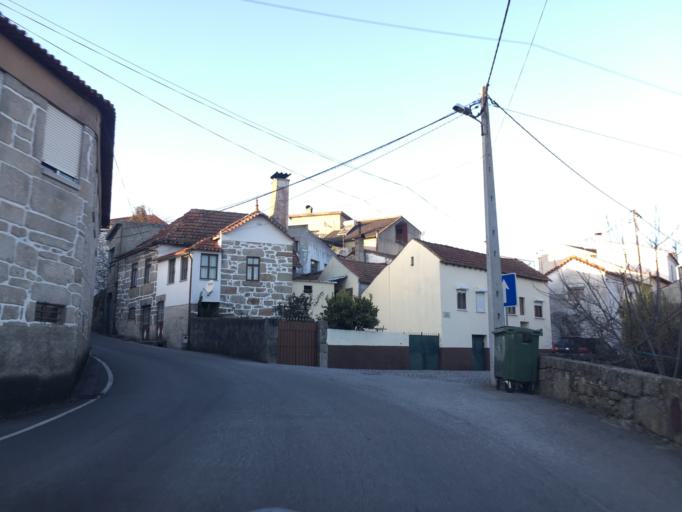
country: PT
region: Viseu
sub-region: Concelho de Carregal do Sal
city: Carregal do Sal
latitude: 40.4715
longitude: -7.9758
